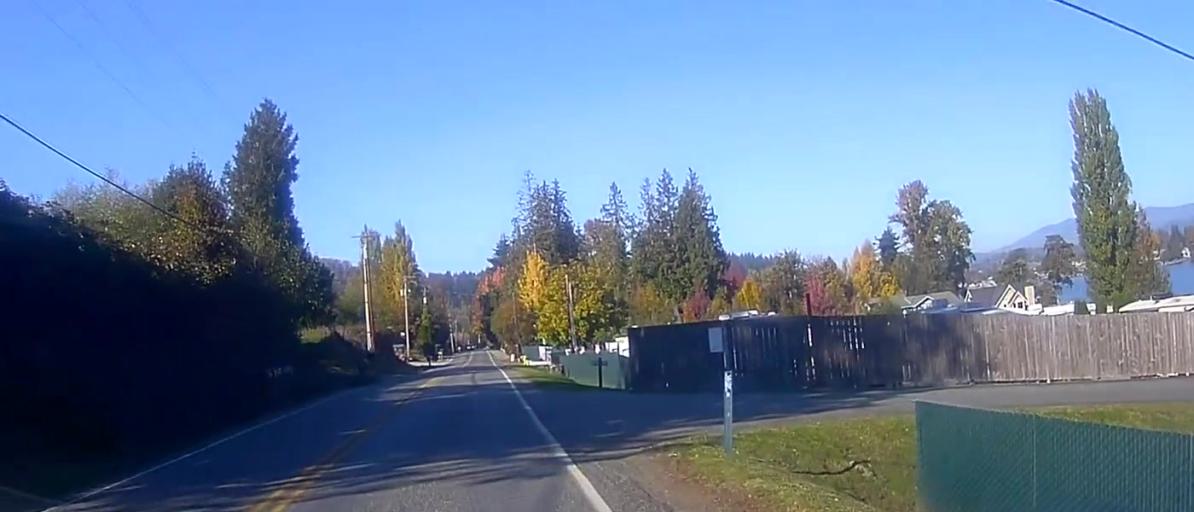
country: US
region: Washington
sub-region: Skagit County
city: Big Lake
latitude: 48.3859
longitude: -122.2427
